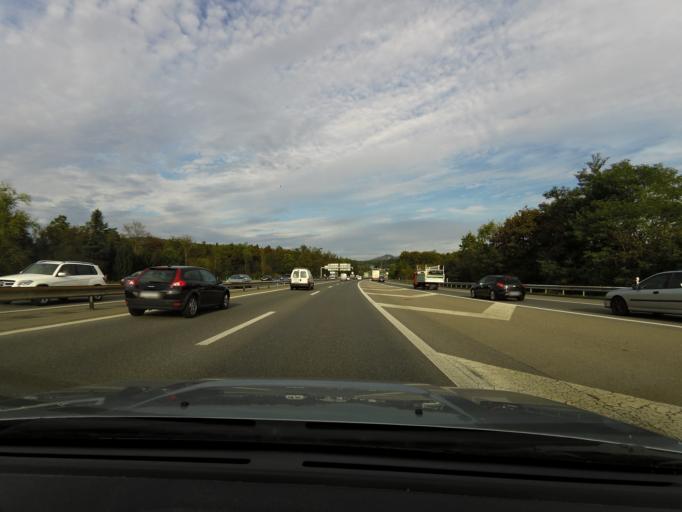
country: CH
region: Aargau
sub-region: Bezirk Baden
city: Birmenstorf
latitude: 47.4479
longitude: 8.2504
